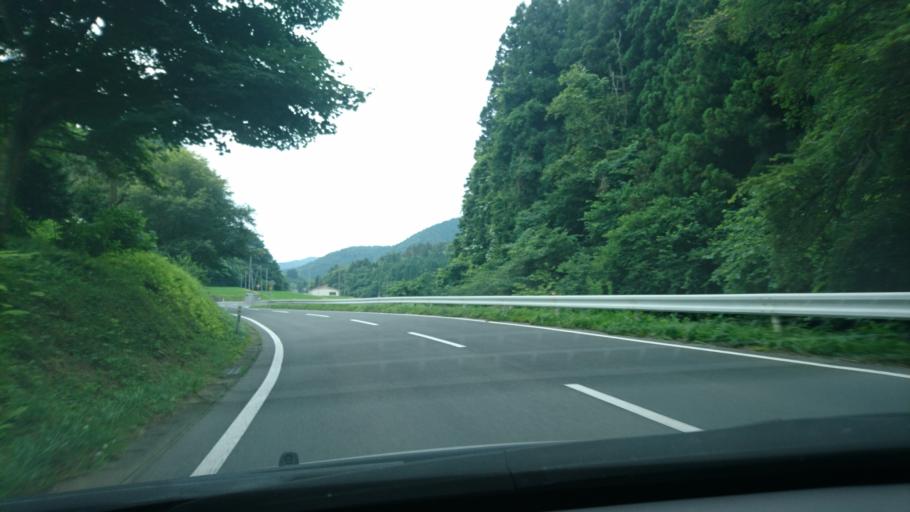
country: JP
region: Iwate
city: Ichinoseki
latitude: 38.8648
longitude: 141.4248
